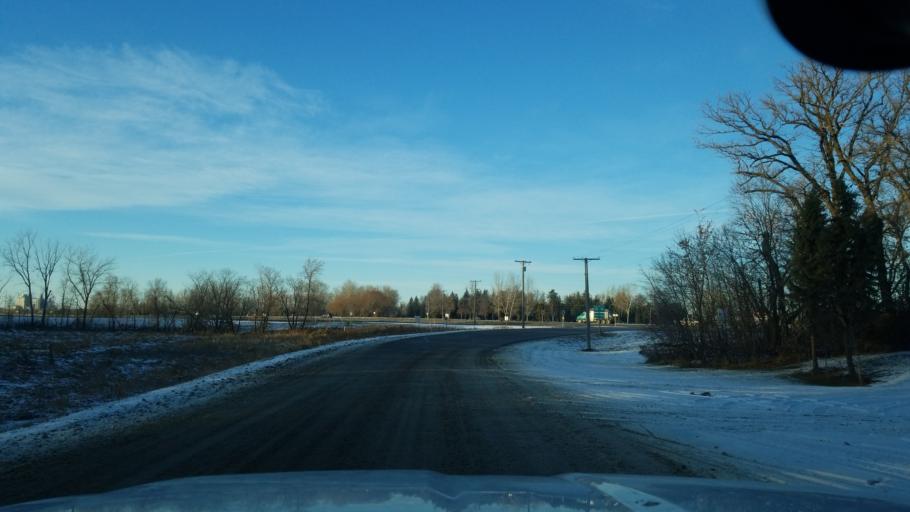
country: CA
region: Manitoba
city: Portage la Prairie
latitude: 49.9535
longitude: -98.3285
